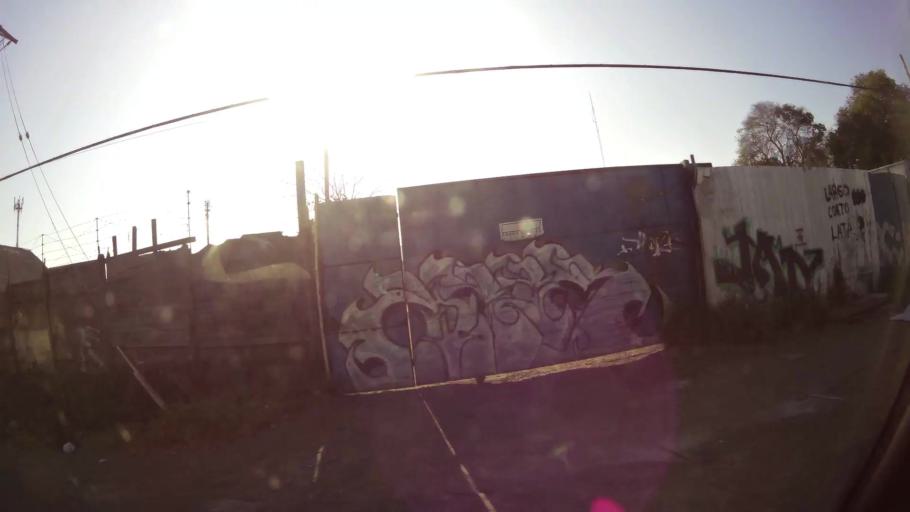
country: CL
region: Santiago Metropolitan
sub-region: Provincia de Santiago
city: Santiago
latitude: -33.4735
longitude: -70.6319
